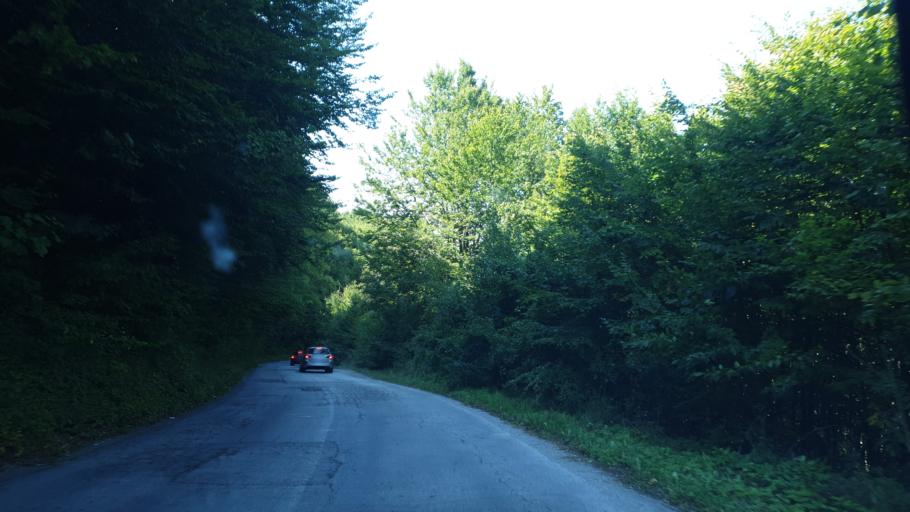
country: RS
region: Central Serbia
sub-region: Zlatiborski Okrug
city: Cajetina
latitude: 43.7093
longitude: 19.8398
